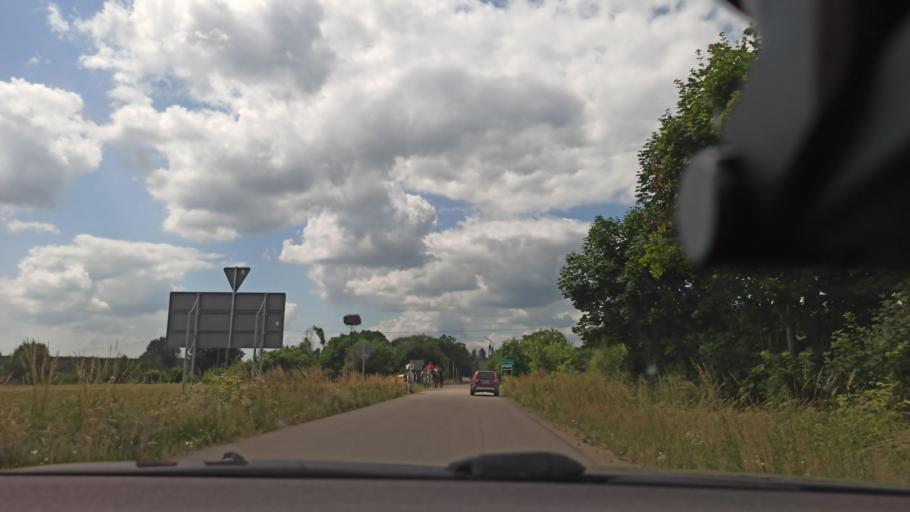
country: PL
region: Podlasie
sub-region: Powiat bialostocki
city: Turosn Koscielna
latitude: 53.0192
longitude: 23.0107
